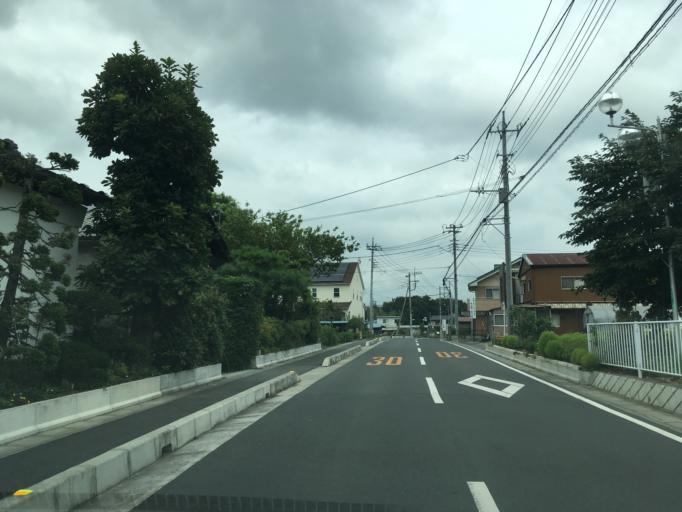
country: JP
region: Saitama
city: Chichibu
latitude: 35.9922
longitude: 139.1039
